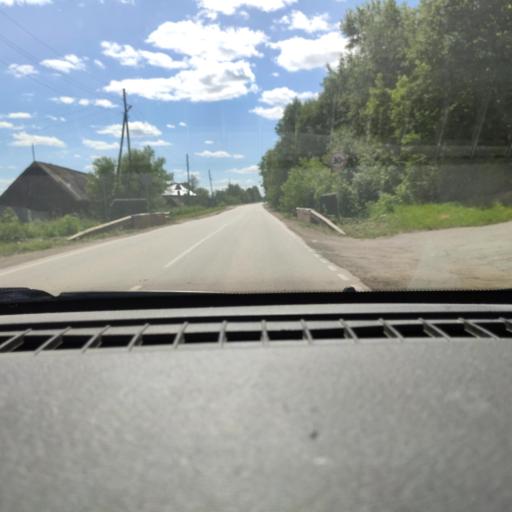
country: RU
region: Perm
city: Chaykovskaya
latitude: 58.1100
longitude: 55.5814
